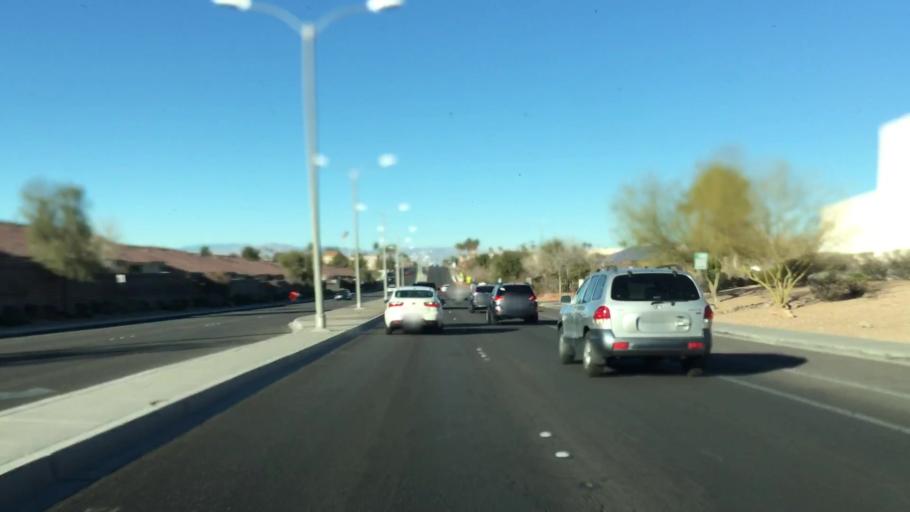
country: US
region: Nevada
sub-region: Clark County
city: Whitney
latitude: 36.0366
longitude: -115.1001
